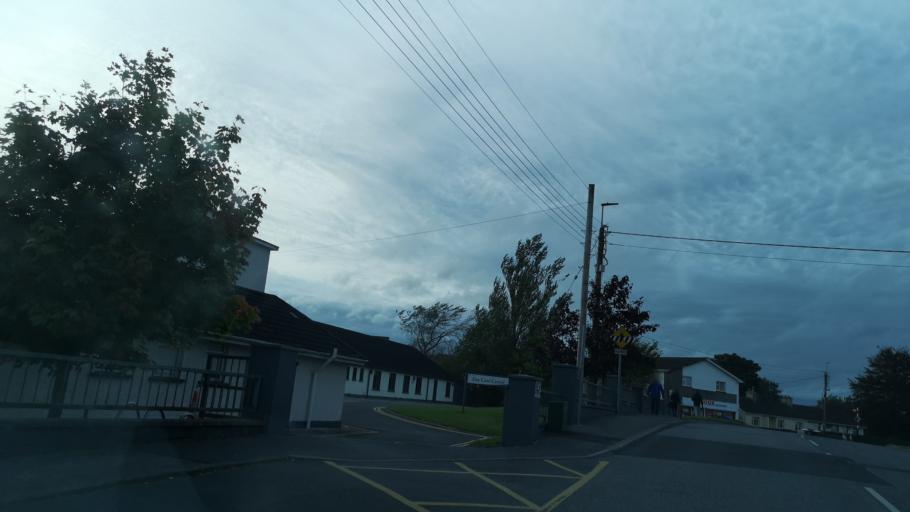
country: IE
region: Leinster
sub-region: An Iarmhi
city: Athlone
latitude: 53.4313
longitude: -7.9458
